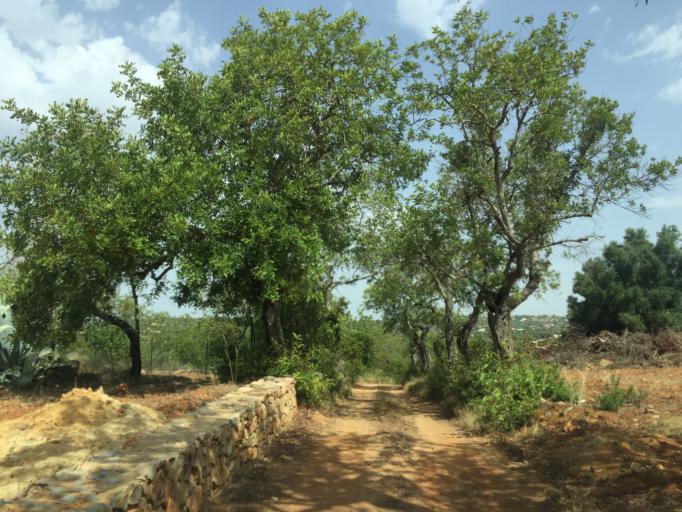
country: PT
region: Faro
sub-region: Loule
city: Boliqueime
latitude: 37.1307
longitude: -8.1338
